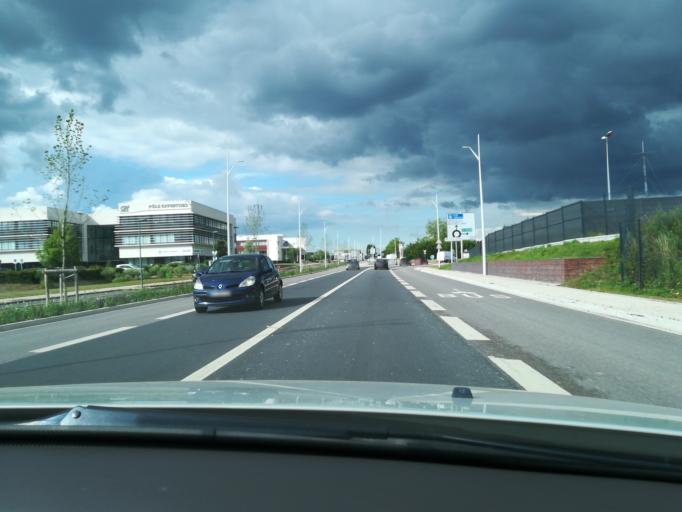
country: FR
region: Haute-Normandie
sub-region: Departement de la Seine-Maritime
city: Isneauville
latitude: 49.4890
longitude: 1.1410
